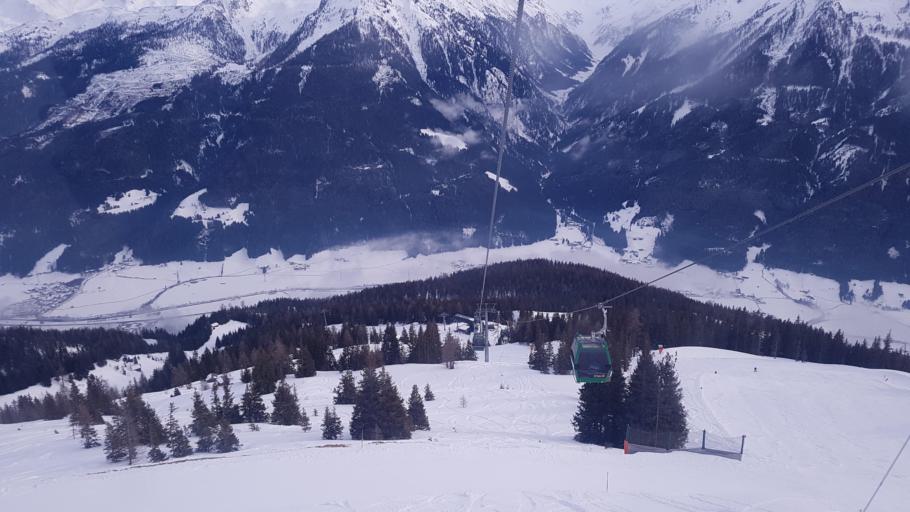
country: AT
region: Salzburg
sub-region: Politischer Bezirk Zell am See
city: Neukirchen am Grossvenediger
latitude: 47.2767
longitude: 12.2993
